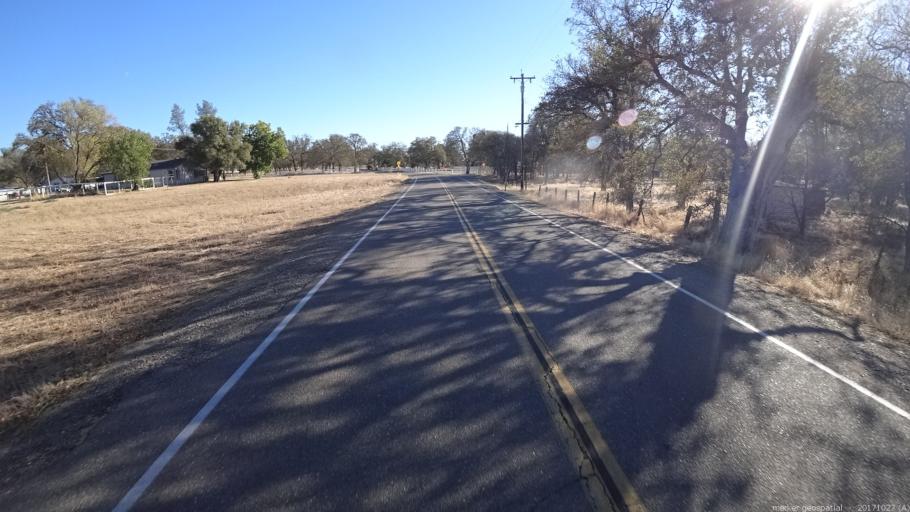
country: US
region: California
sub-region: Shasta County
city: Palo Cedro
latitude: 40.5646
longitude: -122.1913
